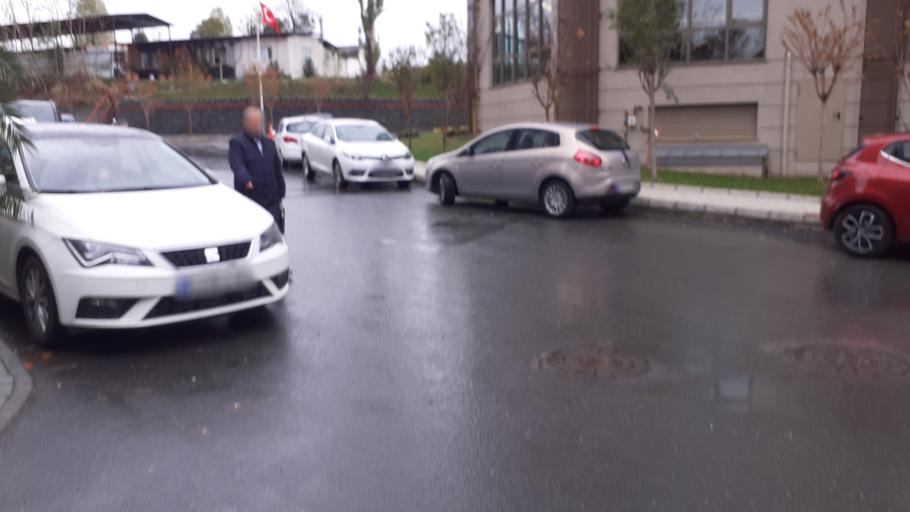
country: TR
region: Istanbul
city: Bahcelievler
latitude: 40.9901
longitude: 28.8354
